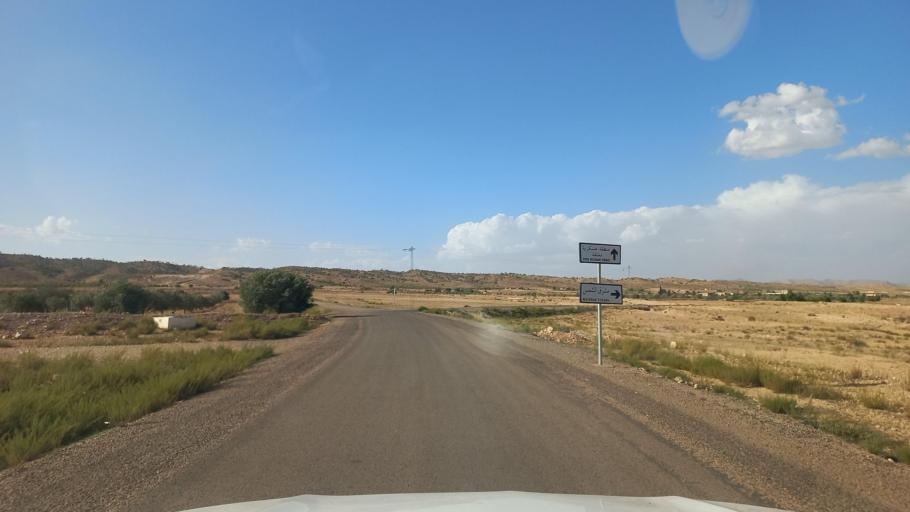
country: TN
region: Al Qasrayn
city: Sbiba
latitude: 35.3481
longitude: 8.9890
